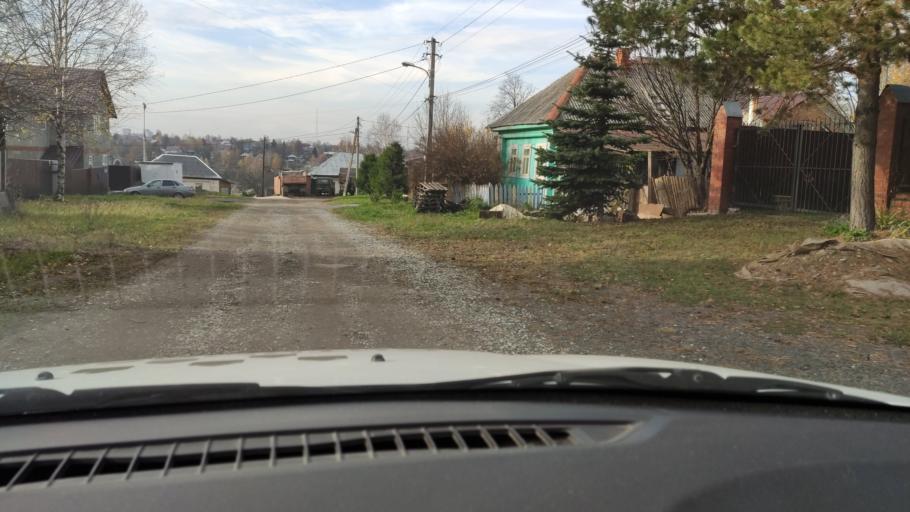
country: RU
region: Perm
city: Perm
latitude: 58.0344
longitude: 56.3432
